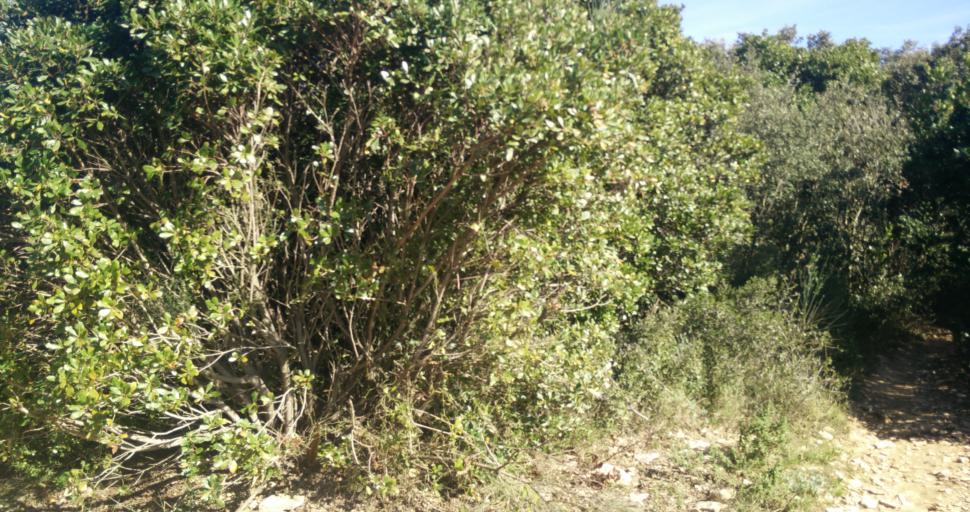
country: FR
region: Languedoc-Roussillon
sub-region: Departement du Gard
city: Calvisson
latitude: 43.8256
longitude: 4.1663
